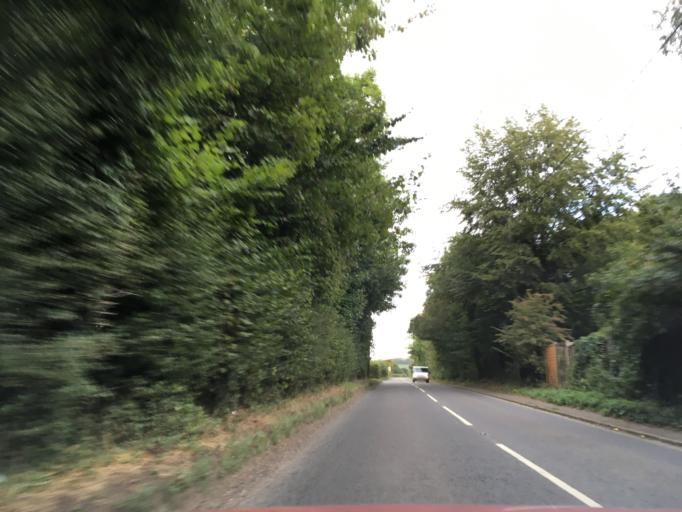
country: GB
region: England
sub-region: Wiltshire
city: Devizes
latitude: 51.3716
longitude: -2.0357
